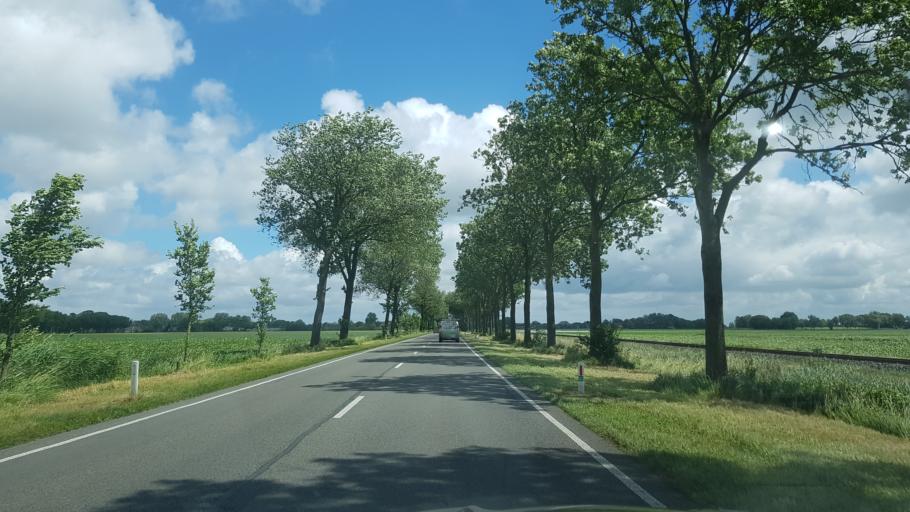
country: NL
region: Groningen
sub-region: Gemeente Bedum
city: Bedum
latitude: 53.4064
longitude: 6.6405
